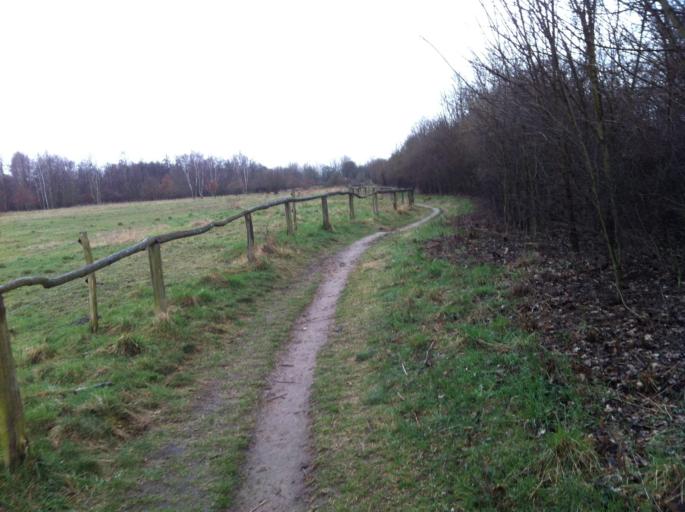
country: DE
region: Berlin
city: Karow
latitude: 52.6265
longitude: 13.4604
